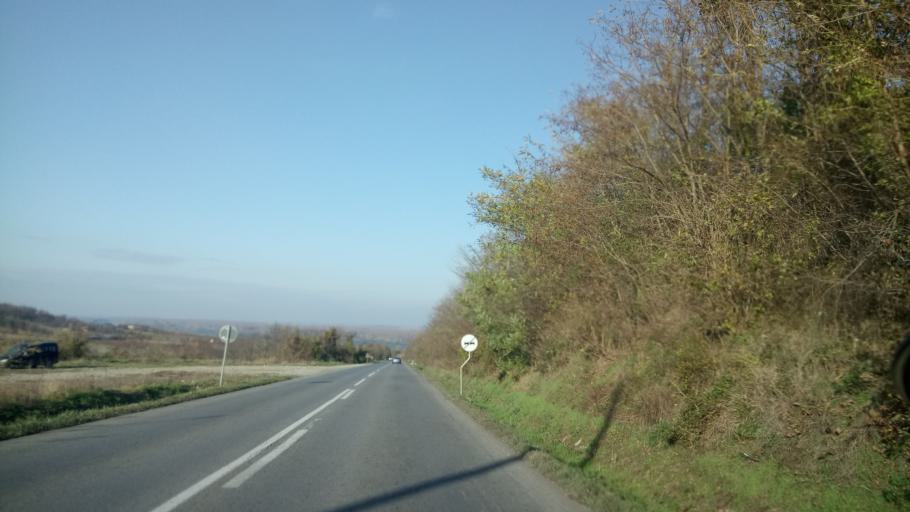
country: RS
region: Autonomna Pokrajina Vojvodina
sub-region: Juznobacki Okrug
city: Sremski Karlovci
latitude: 45.1816
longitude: 19.9534
